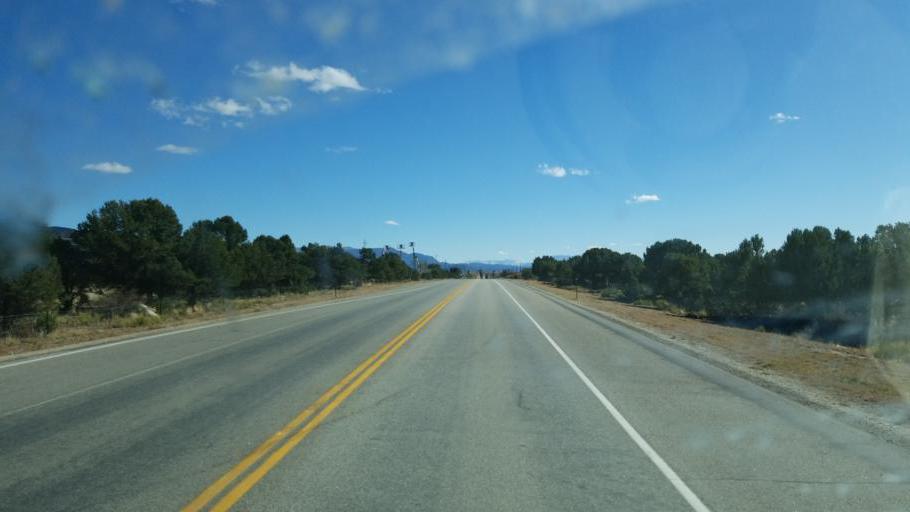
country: US
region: Colorado
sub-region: Chaffee County
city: Buena Vista
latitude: 38.8564
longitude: -106.1419
